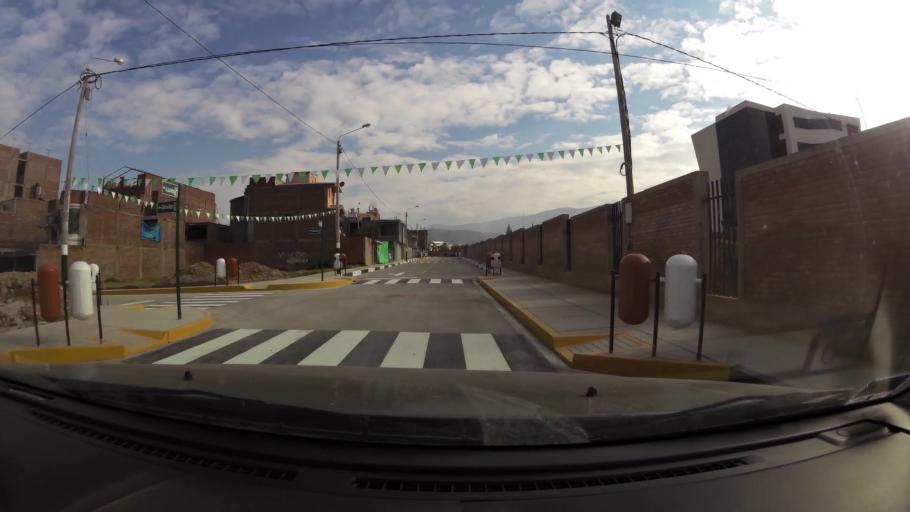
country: PE
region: Junin
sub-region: Provincia de Huancayo
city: Huancayo
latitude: -12.0449
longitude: -75.1911
